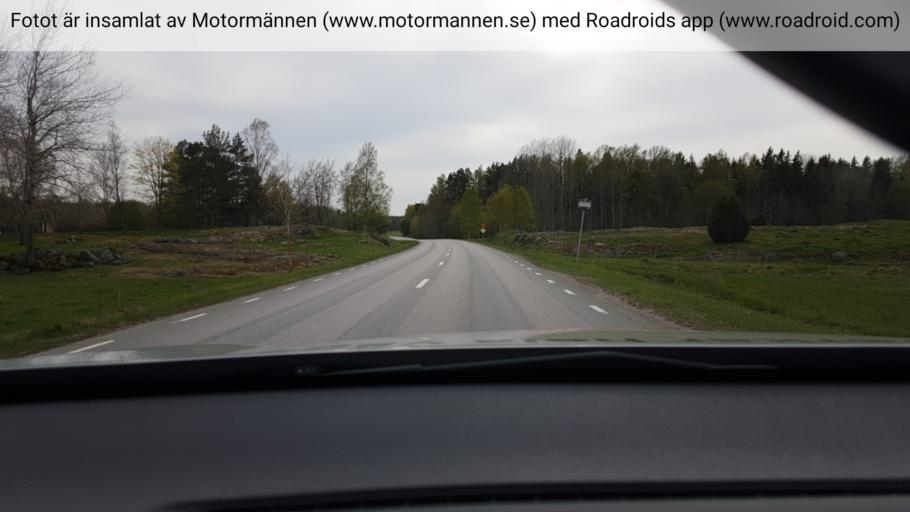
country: SE
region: Stockholm
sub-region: Norrtalje Kommun
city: Nykvarn
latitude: 59.9276
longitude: 18.1118
